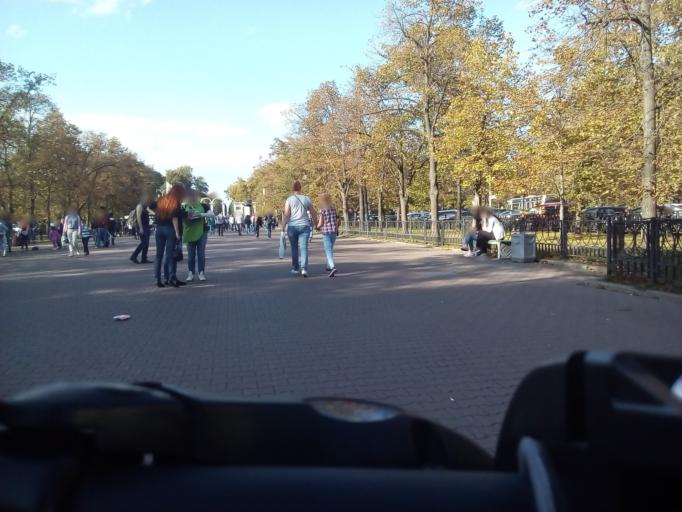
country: RU
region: Moscow
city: Sokol'niki
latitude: 55.7910
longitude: 37.6788
